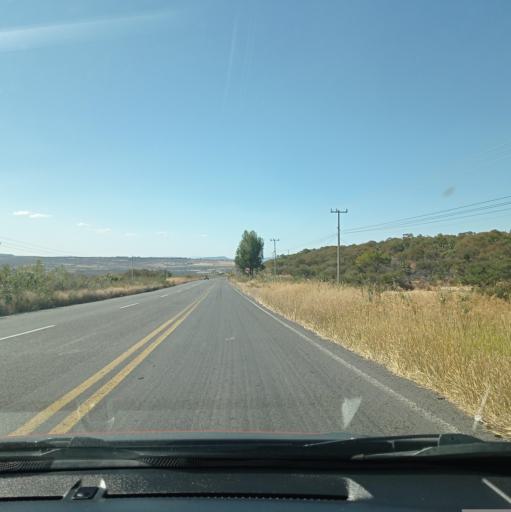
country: MX
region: Jalisco
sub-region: San Julian
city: Colonia Veintitres de Mayo
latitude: 21.0086
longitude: -102.2646
